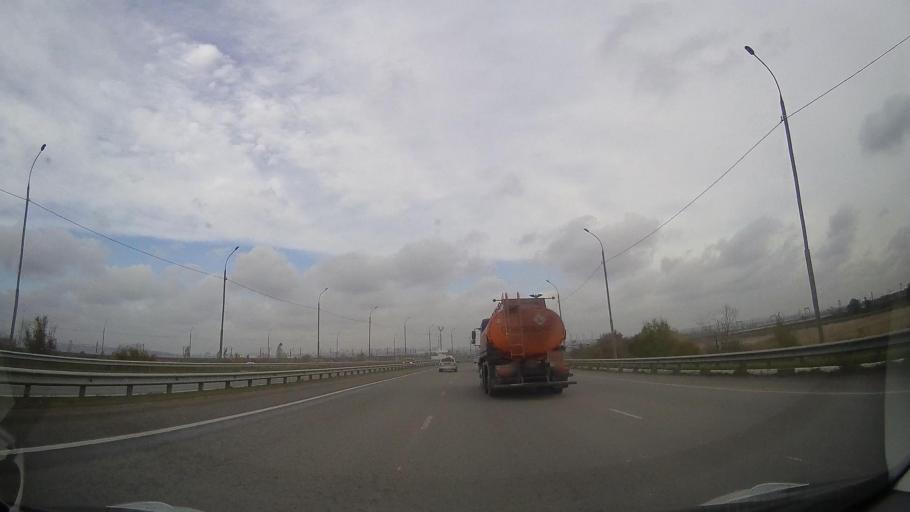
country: RU
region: Rostov
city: Bataysk
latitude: 47.1609
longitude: 39.7410
